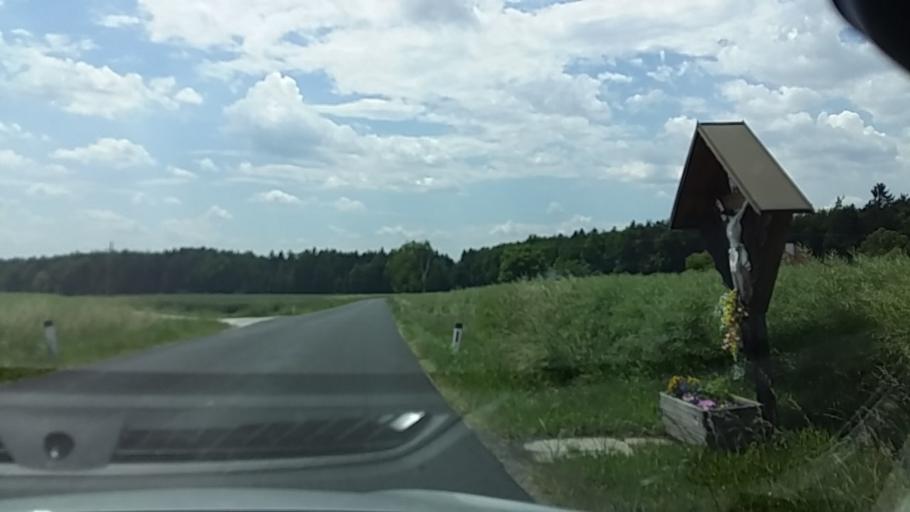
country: AT
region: Styria
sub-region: Politischer Bezirk Hartberg-Fuerstenfeld
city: Bad Blumau
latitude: 47.1138
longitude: 15.9971
